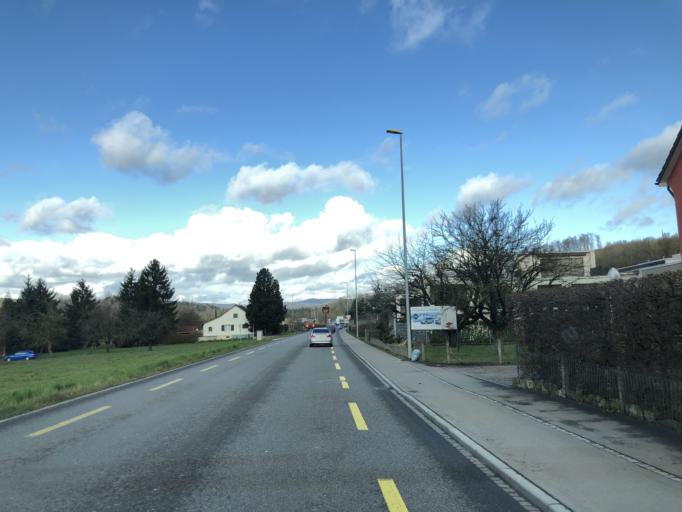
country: CH
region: Aargau
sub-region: Bezirk Baden
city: Birmenstorf
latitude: 47.4626
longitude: 8.2431
